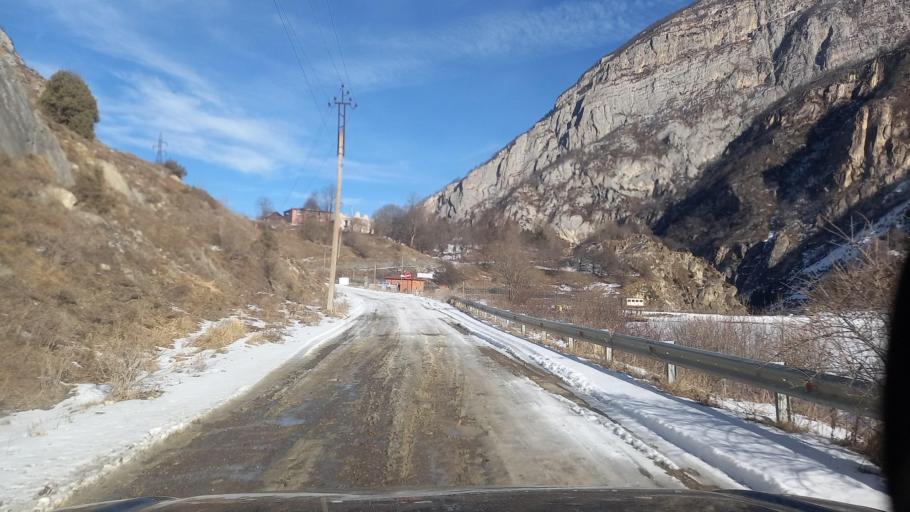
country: RU
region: North Ossetia
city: Verkhniy Fiagdon
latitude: 42.8771
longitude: 44.4485
